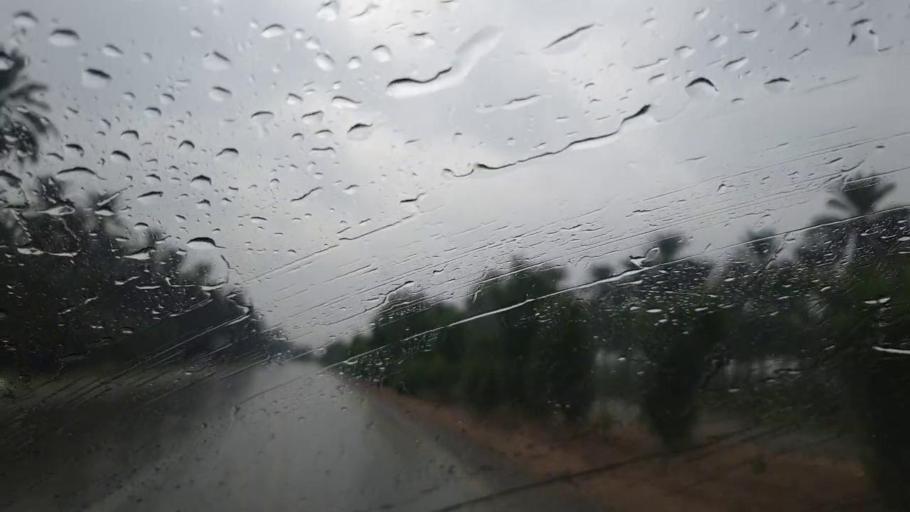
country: PK
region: Sindh
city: Khairpur
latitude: 27.5755
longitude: 68.7525
